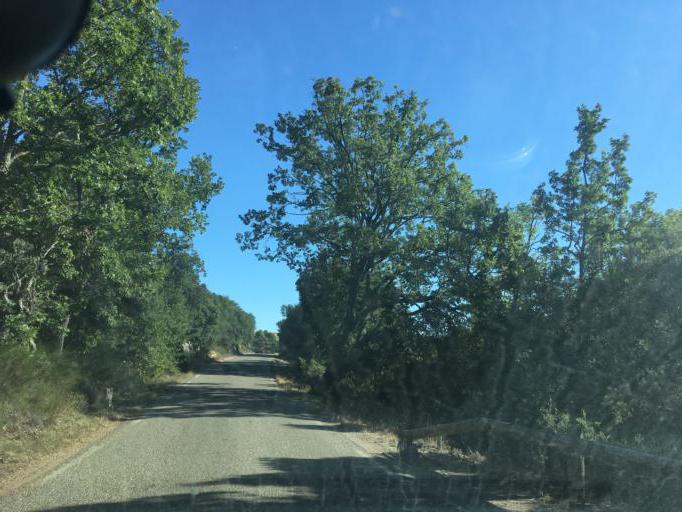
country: FR
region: Provence-Alpes-Cote d'Azur
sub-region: Departement du Var
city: Regusse
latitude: 43.7126
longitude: 6.1411
